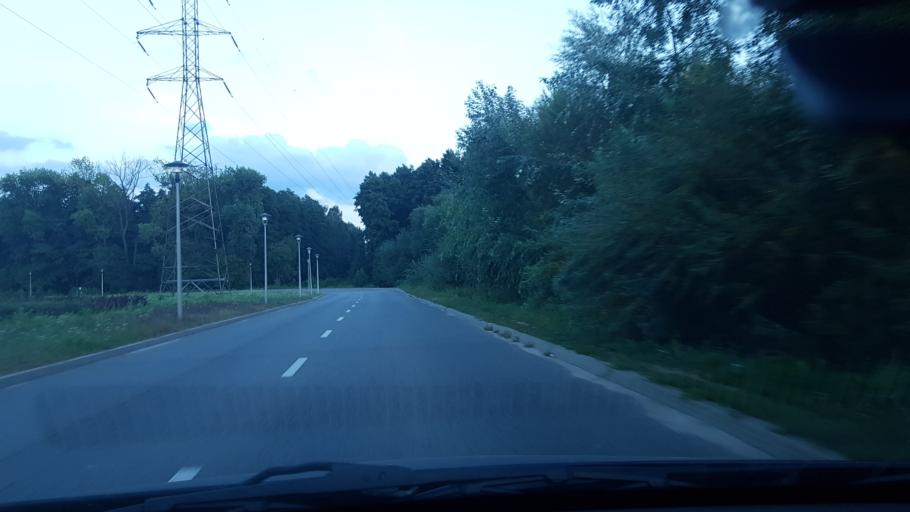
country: PL
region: Masovian Voivodeship
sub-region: Warszawa
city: Targowek
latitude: 52.3023
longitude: 21.0752
